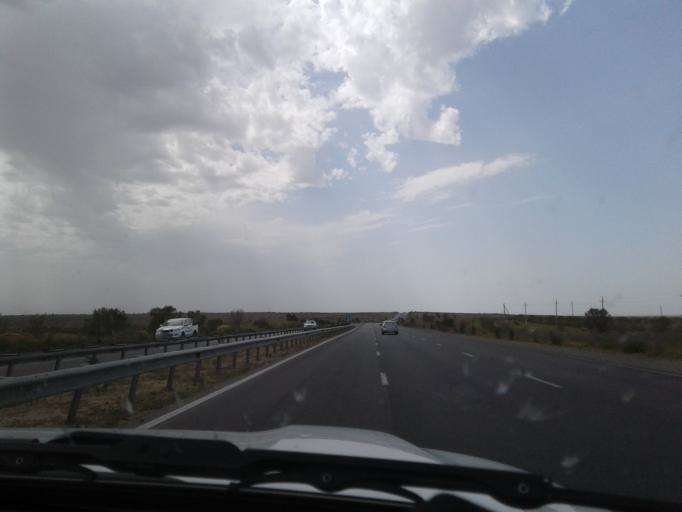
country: TM
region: Ahal
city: Annau
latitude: 37.8721
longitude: 58.6531
